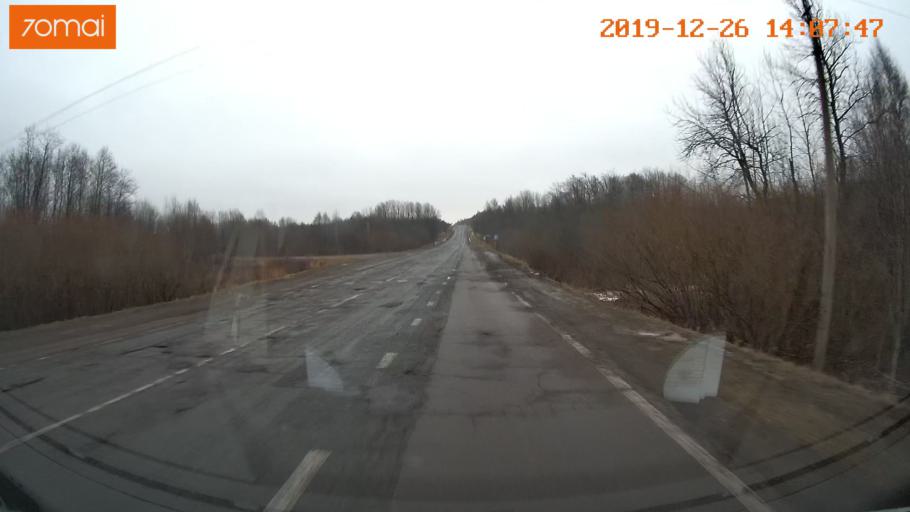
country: RU
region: Jaroslavl
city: Poshekhon'ye
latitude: 58.5091
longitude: 38.8971
